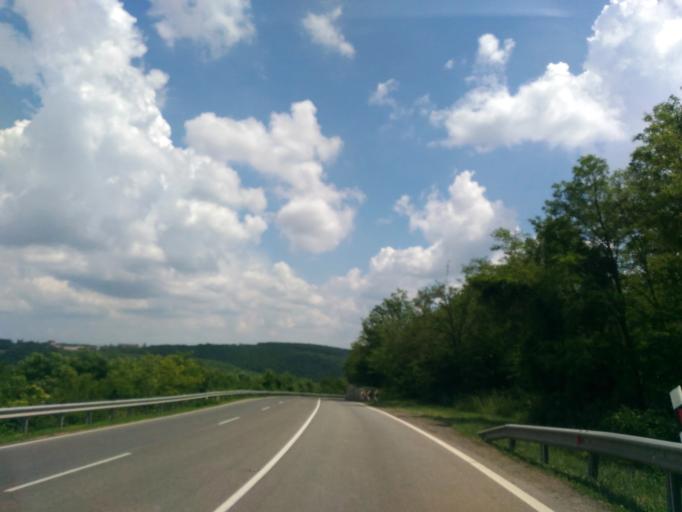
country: HU
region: Baranya
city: Pecs
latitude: 46.1275
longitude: 18.2552
